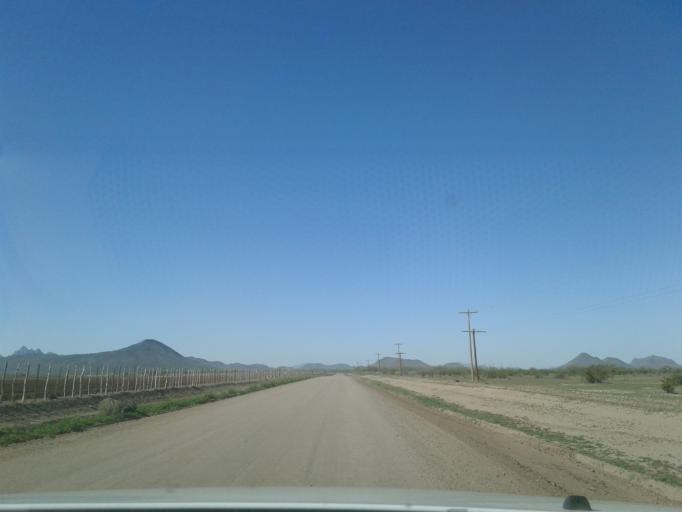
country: US
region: Arizona
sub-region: Pima County
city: Avra Valley
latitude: 32.5539
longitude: -111.3818
